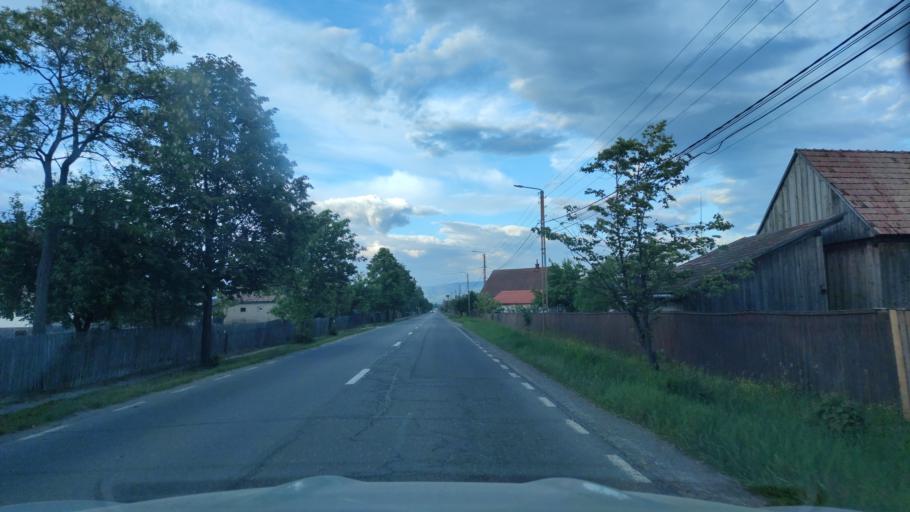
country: RO
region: Harghita
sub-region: Comuna Joseni
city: Joseni
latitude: 46.6960
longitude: 25.4609
